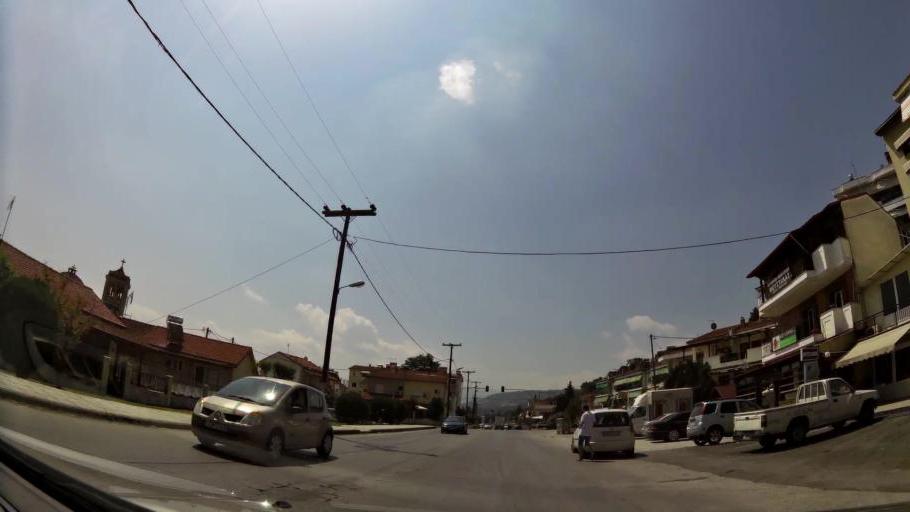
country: GR
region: Central Macedonia
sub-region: Nomos Imathias
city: Veroia
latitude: 40.5309
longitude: 22.2077
